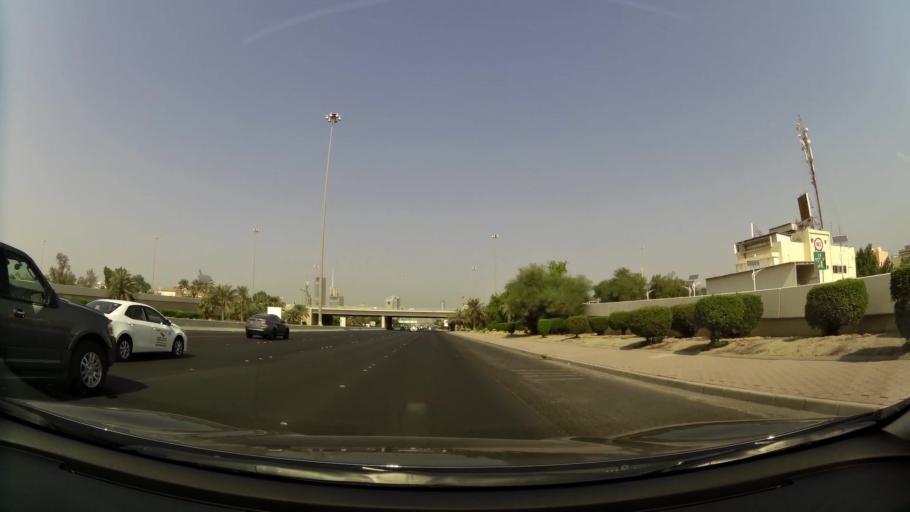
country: KW
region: Al Asimah
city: Ad Dasmah
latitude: 29.3490
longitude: 47.9951
